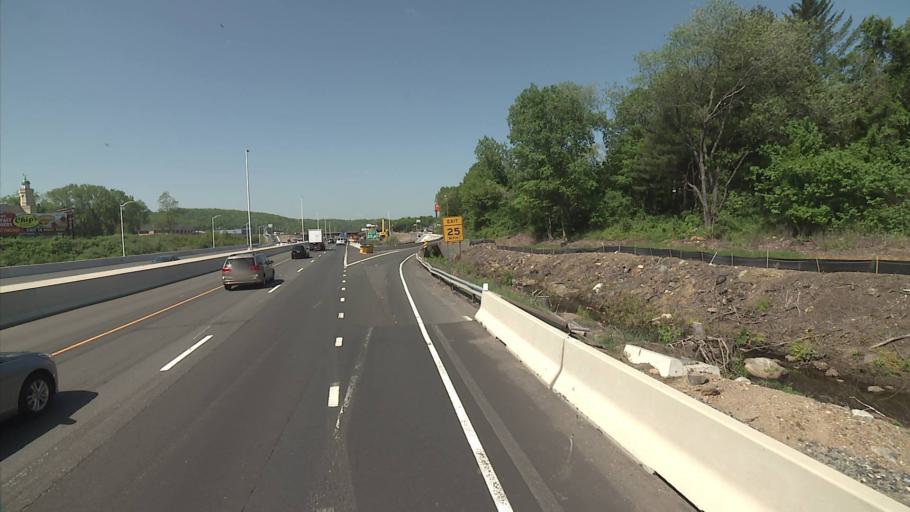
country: US
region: Connecticut
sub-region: New Haven County
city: Prospect
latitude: 41.5427
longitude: -72.9899
